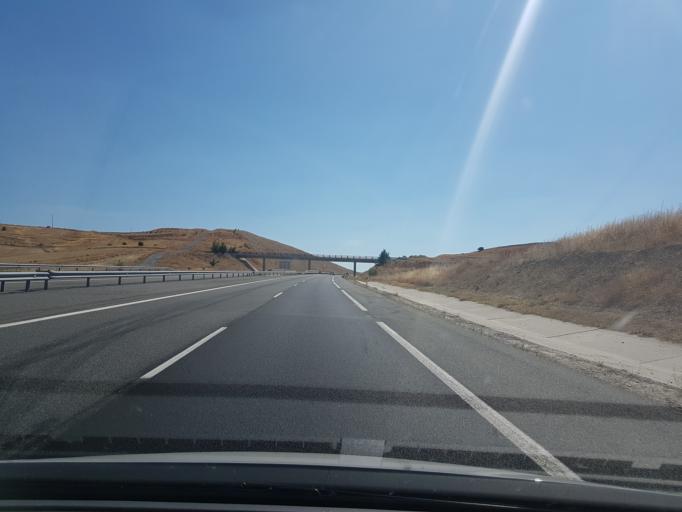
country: ES
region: Castille and Leon
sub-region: Provincia de Avila
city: Penalba de Avila
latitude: 40.7666
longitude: -4.7544
